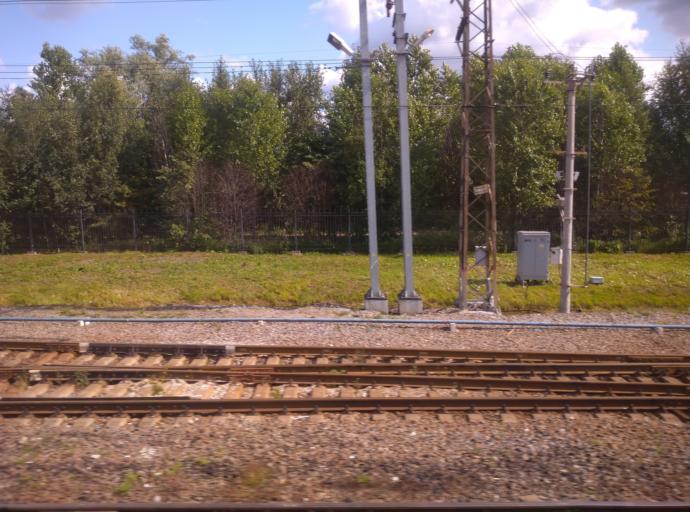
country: RU
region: St.-Petersburg
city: Kolpino
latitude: 59.7527
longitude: 30.6099
